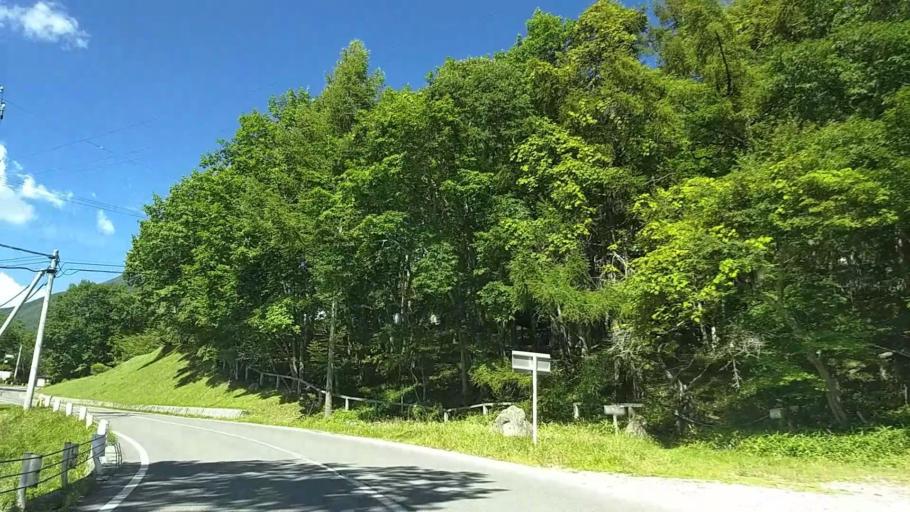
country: JP
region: Nagano
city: Chino
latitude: 36.0636
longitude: 138.2892
